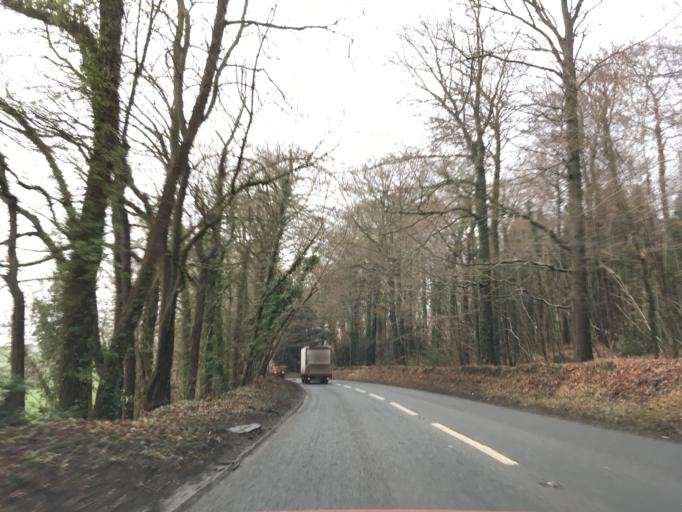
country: GB
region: England
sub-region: Gloucestershire
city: Tetbury
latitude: 51.6666
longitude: -2.1037
